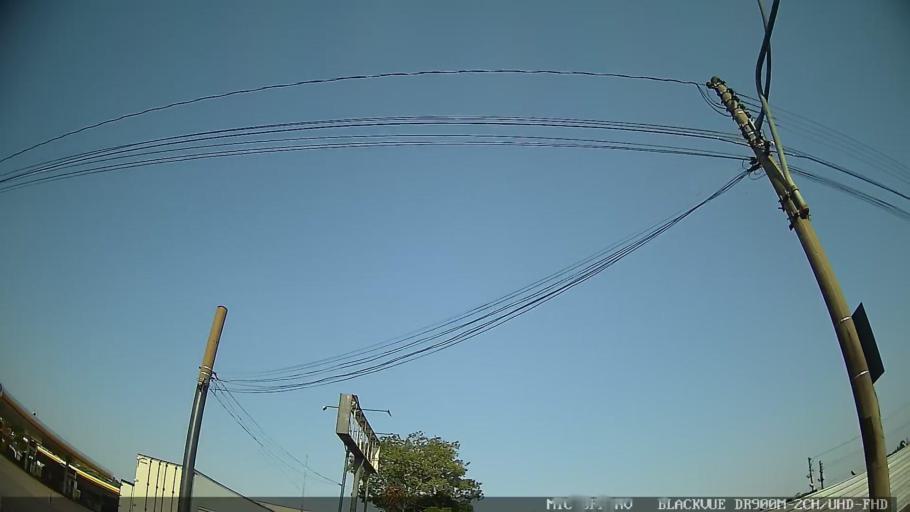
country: BR
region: Sao Paulo
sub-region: Itatiba
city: Itatiba
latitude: -23.0203
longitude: -46.8423
